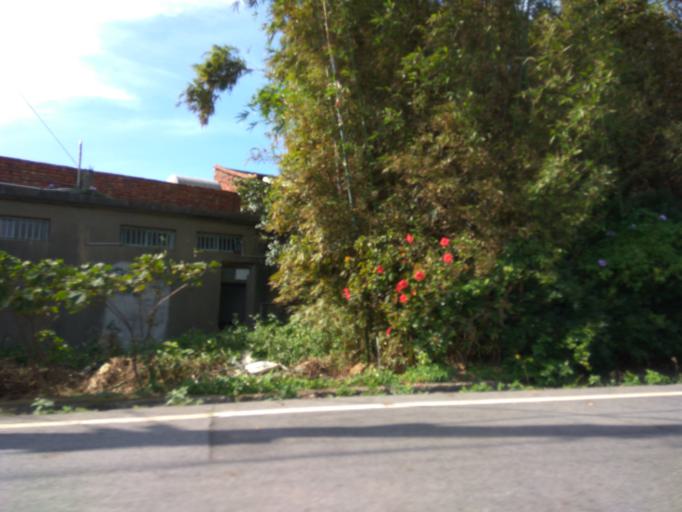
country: TW
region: Taiwan
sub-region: Hsinchu
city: Zhubei
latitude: 25.0105
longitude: 121.0765
